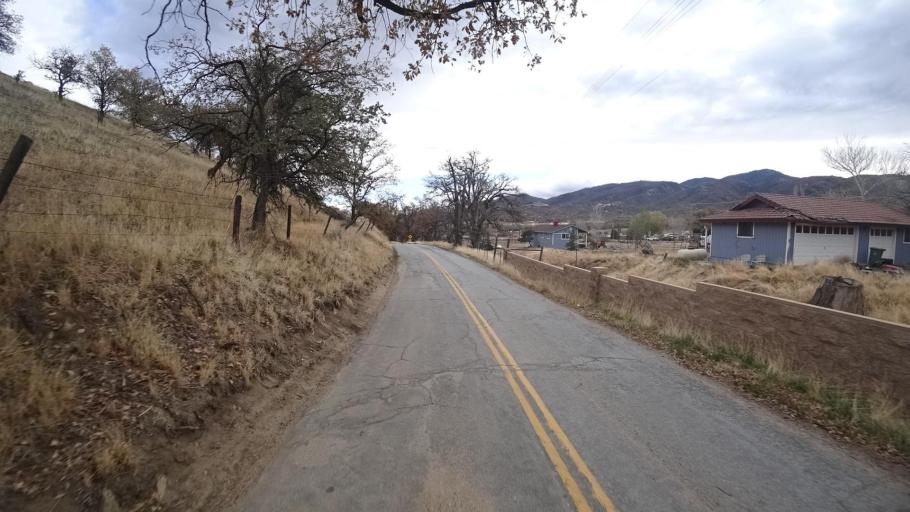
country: US
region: California
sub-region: Kern County
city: Golden Hills
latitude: 35.1127
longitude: -118.5178
